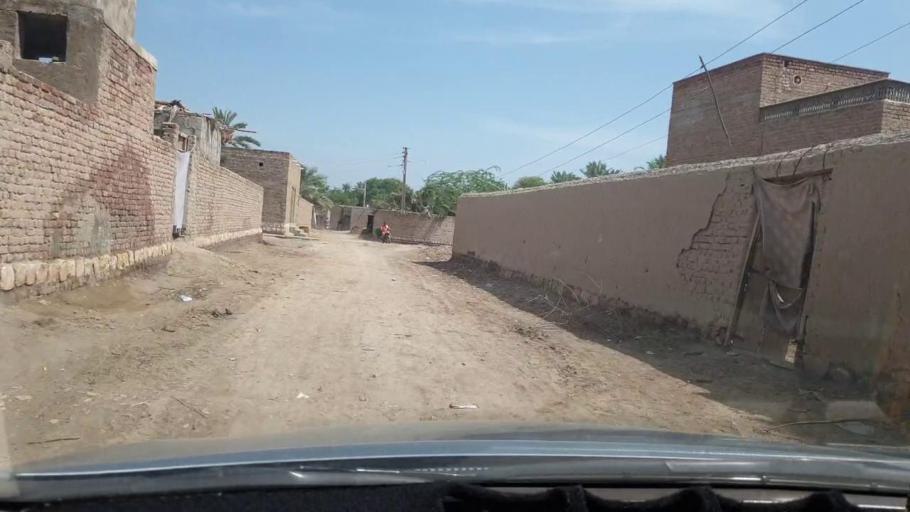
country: PK
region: Sindh
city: Khairpur
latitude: 27.4745
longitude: 68.7411
